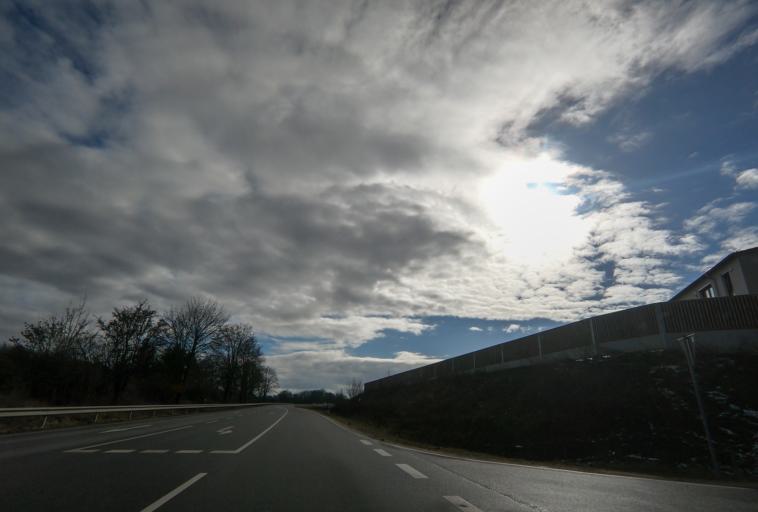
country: DE
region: Bavaria
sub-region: Upper Palatinate
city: Kofering
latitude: 48.9330
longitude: 12.2039
